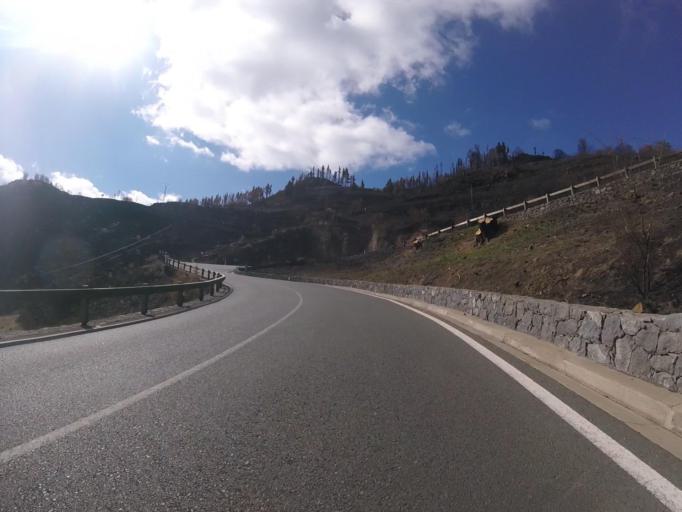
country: ES
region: Canary Islands
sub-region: Provincia de Las Palmas
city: Tejeda
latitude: 28.0050
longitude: -15.5957
